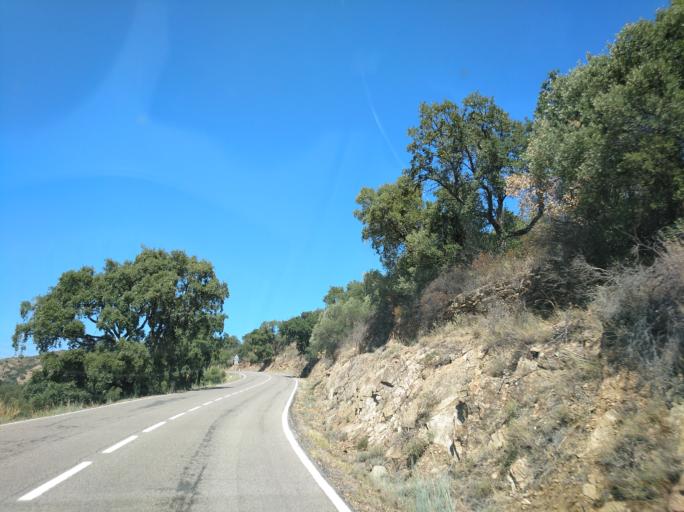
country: ES
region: Catalonia
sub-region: Provincia de Girona
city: Pau
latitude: 42.3309
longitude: 3.1166
